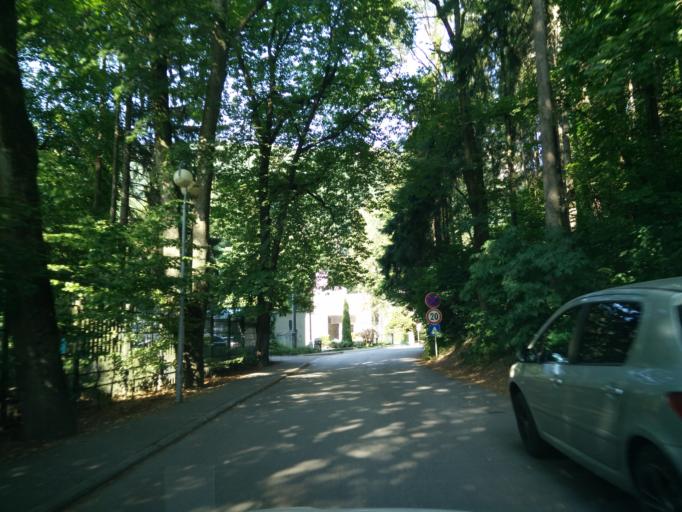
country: SK
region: Zilinsky
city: Rajec
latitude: 49.1310
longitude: 18.6847
